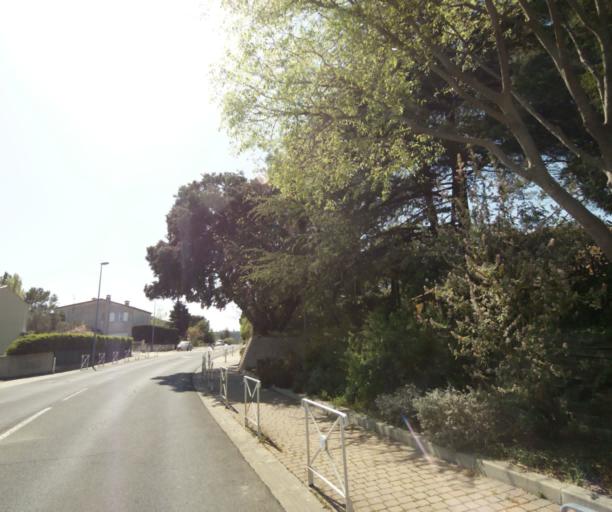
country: FR
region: Languedoc-Roussillon
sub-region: Departement de l'Herault
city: Grabels
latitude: 43.6512
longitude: 3.8073
